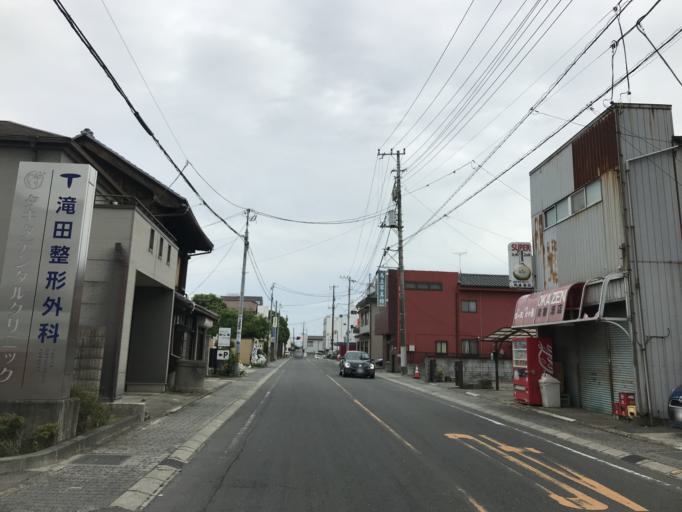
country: JP
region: Ibaraki
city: Ishioka
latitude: 36.1924
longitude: 140.2723
